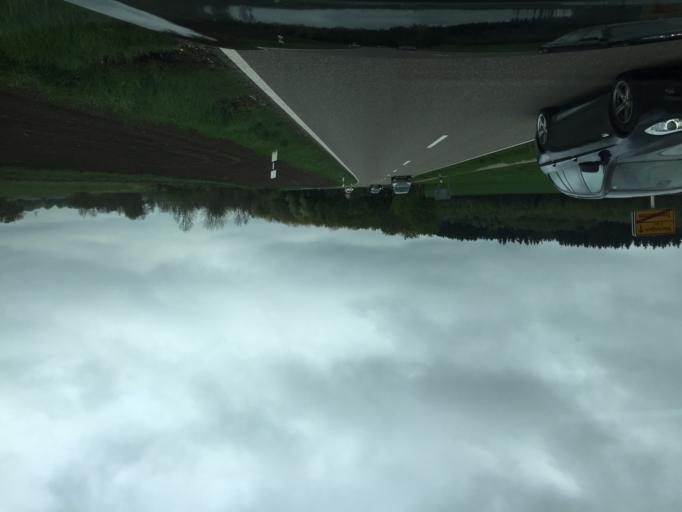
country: DE
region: Bavaria
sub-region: Swabia
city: Buttenwiesen
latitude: 48.5788
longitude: 10.7141
